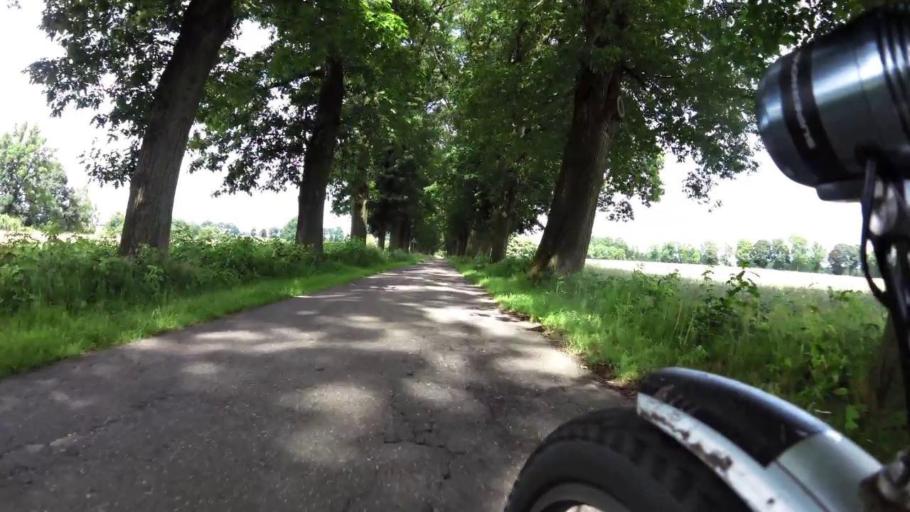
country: PL
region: West Pomeranian Voivodeship
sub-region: Powiat bialogardzki
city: Bialogard
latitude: 53.9489
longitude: 15.9944
